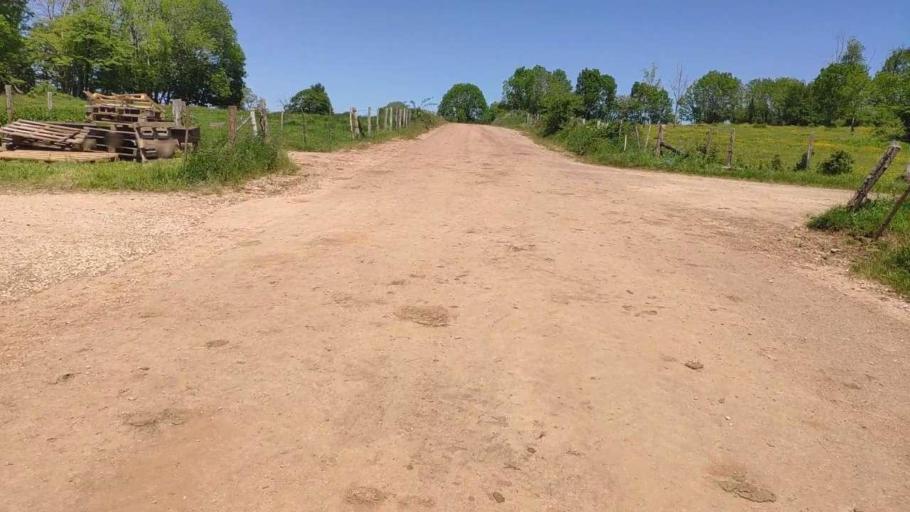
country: FR
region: Franche-Comte
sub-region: Departement du Jura
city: Poligny
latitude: 46.7673
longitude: 5.6871
